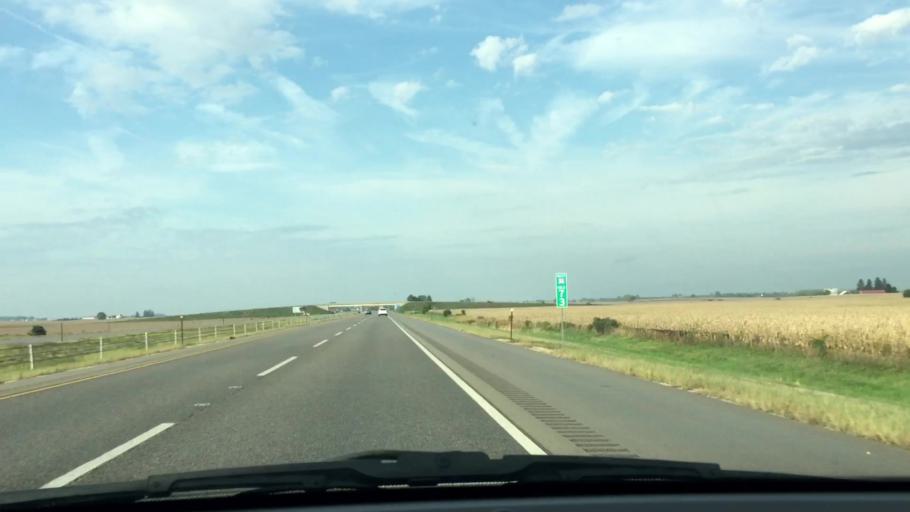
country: US
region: Illinois
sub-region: Ogle County
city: Rochelle
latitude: 41.8836
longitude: -89.1240
